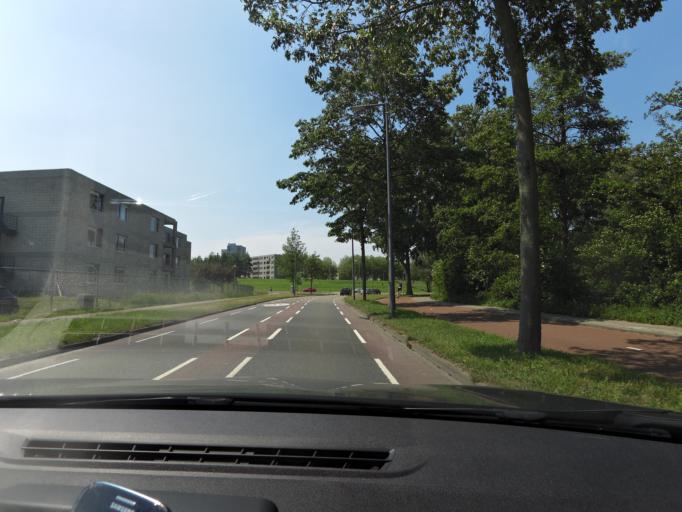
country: NL
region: South Holland
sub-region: Gemeente Rotterdam
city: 's-Gravenland
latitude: 51.9096
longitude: 4.5270
